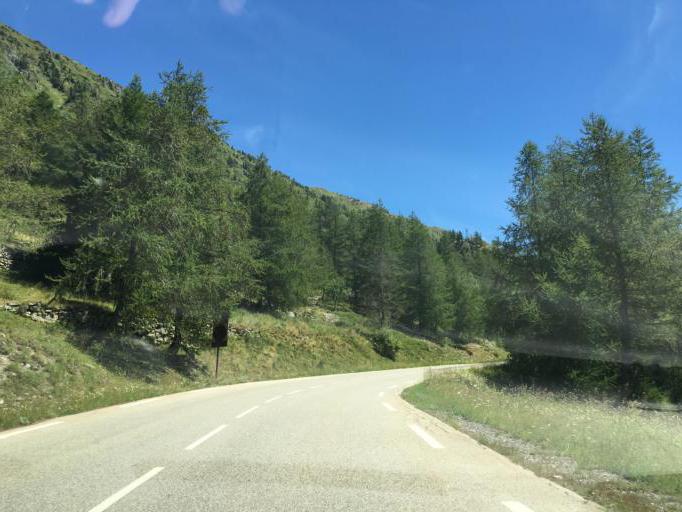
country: IT
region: Piedmont
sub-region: Provincia di Cuneo
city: Vinadio
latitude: 44.2095
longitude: 7.1042
